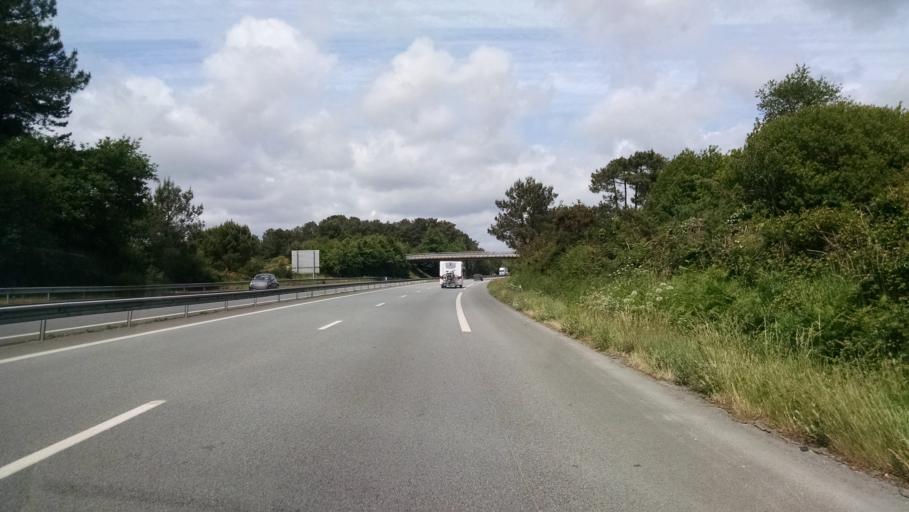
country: FR
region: Brittany
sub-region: Departement du Morbihan
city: Auray
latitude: 47.6874
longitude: -3.0310
